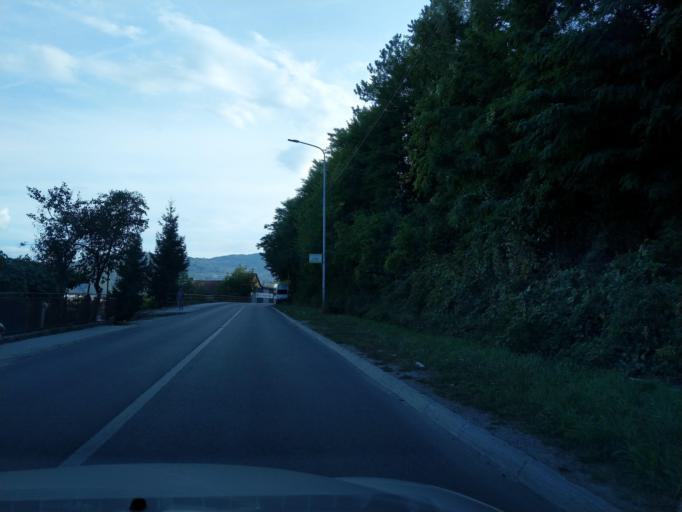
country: RS
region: Central Serbia
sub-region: Zlatiborski Okrug
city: Prijepolje
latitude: 43.3571
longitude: 19.6354
